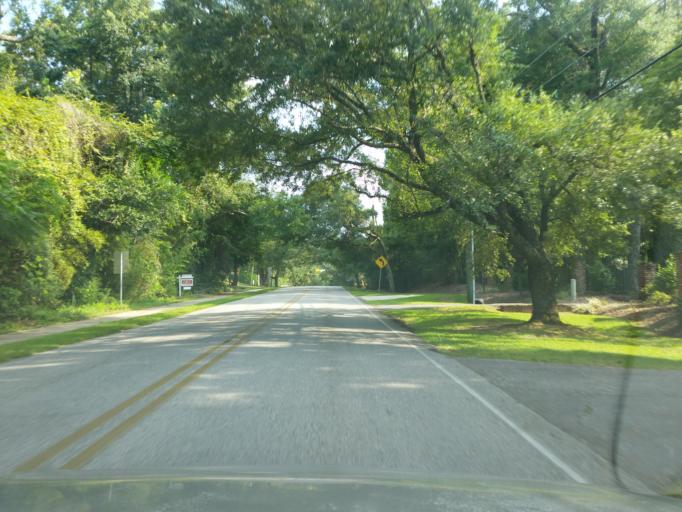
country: US
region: Alabama
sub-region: Baldwin County
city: Fairhope
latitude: 30.5562
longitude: -87.8997
